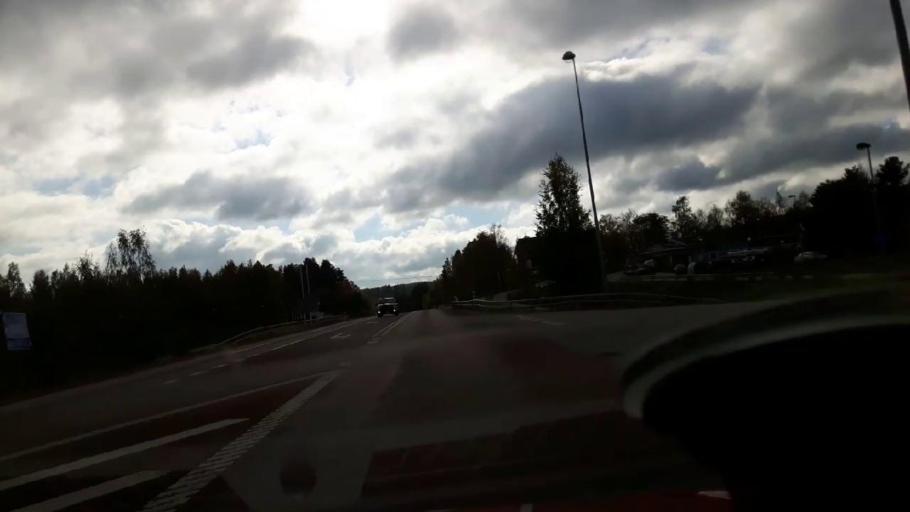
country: SE
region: Gaevleborg
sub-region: Ljusdals Kommun
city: Jaervsoe
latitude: 61.6726
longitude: 16.1453
